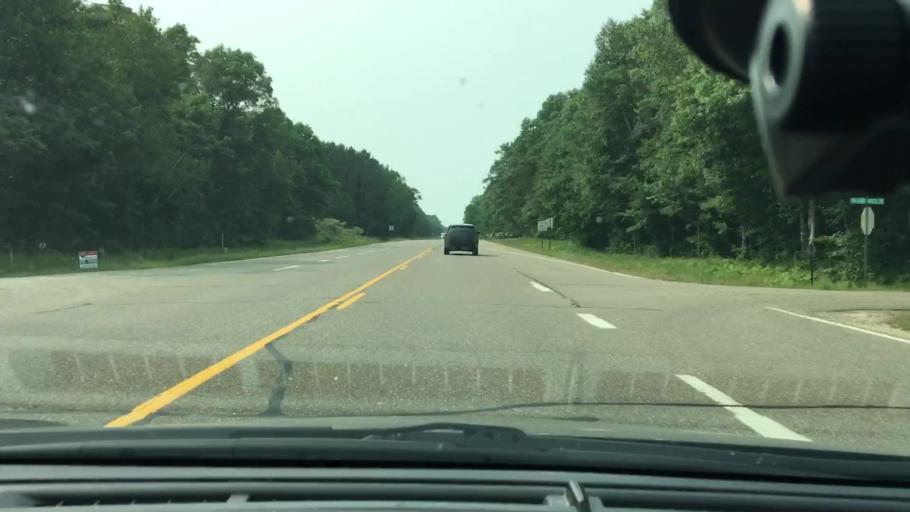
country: US
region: Minnesota
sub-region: Crow Wing County
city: Breezy Point
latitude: 46.5122
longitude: -94.1336
